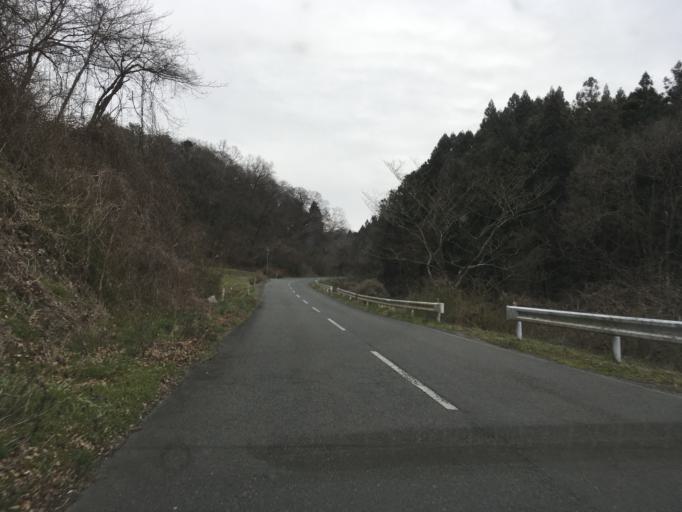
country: JP
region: Iwate
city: Ichinoseki
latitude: 38.7650
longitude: 141.2208
